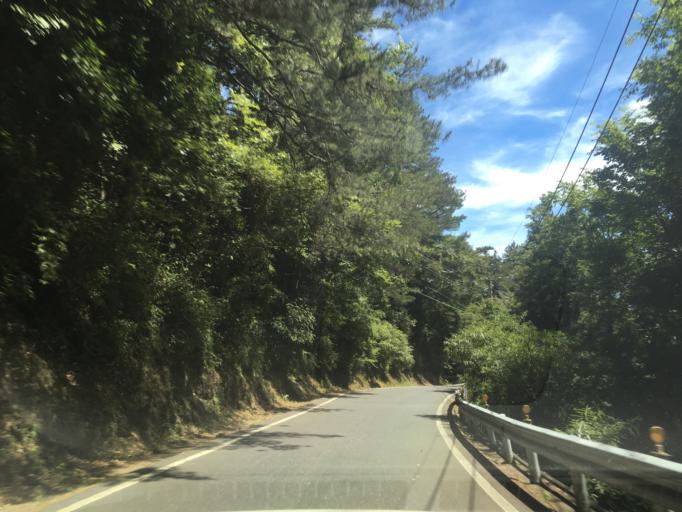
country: TW
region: Taiwan
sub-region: Nantou
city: Puli
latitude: 24.2257
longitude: 121.2563
